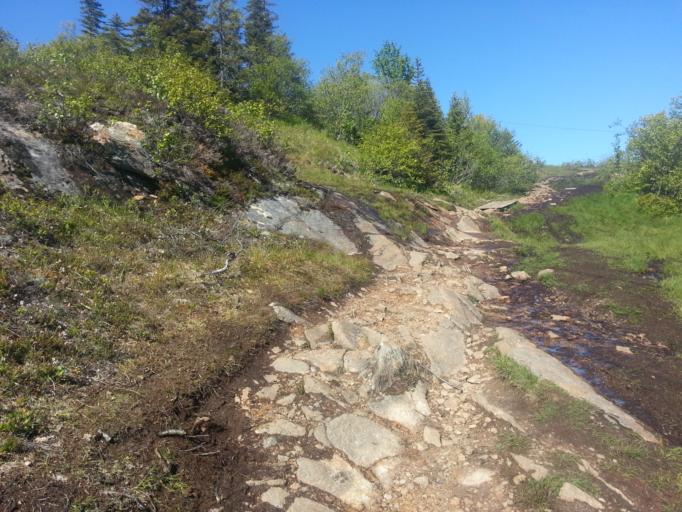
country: NO
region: Sor-Trondelag
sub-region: Melhus
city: Melhus
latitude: 63.4184
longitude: 10.2535
